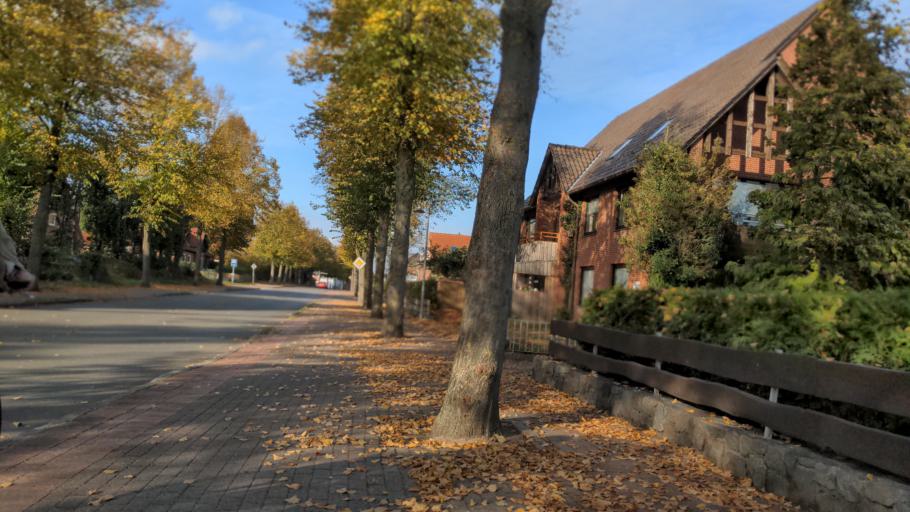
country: DE
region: Schleswig-Holstein
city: Lensahn
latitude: 54.2166
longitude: 10.8835
